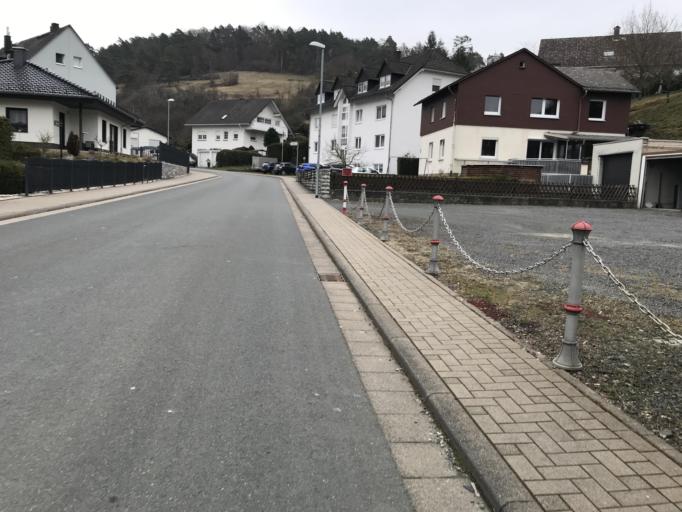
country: DE
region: Hesse
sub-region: Regierungsbezirk Giessen
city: Sinn
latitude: 50.6521
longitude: 8.3337
